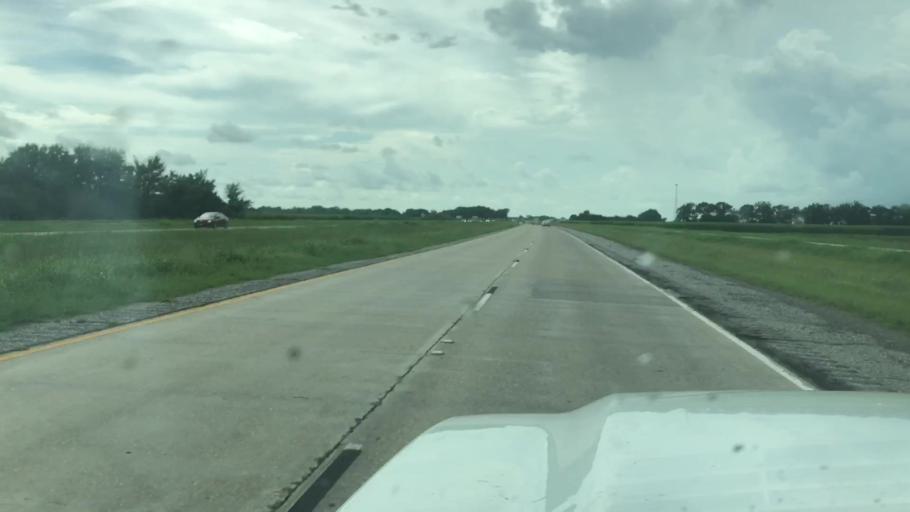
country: US
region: Louisiana
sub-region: Saint Mary Parish
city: Baldwin
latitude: 29.8575
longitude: -91.6125
